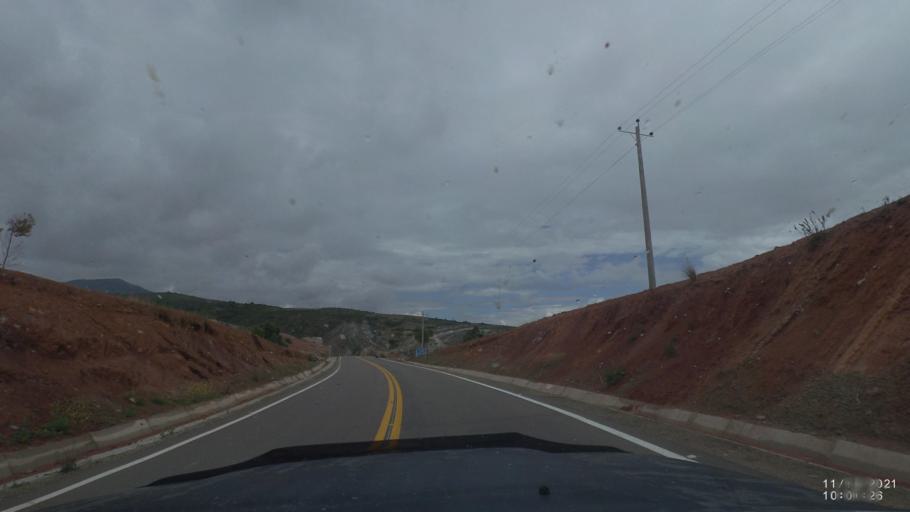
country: BO
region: Cochabamba
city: Cliza
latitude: -17.7284
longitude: -65.9286
